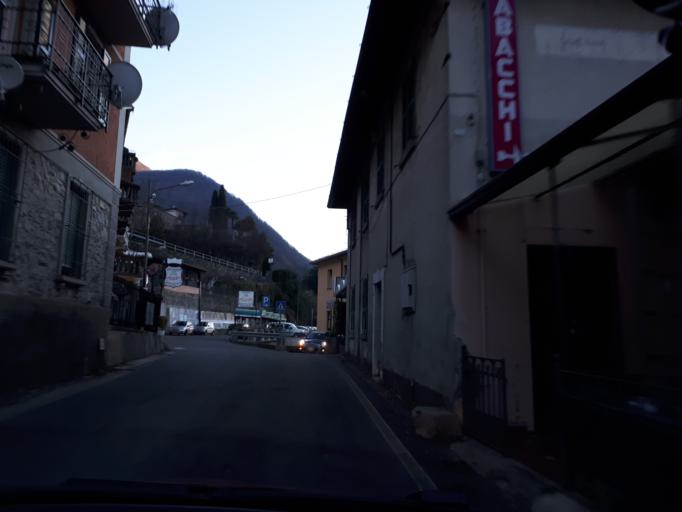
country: IT
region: Lombardy
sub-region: Provincia di Como
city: Nesso
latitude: 45.9147
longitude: 9.1540
